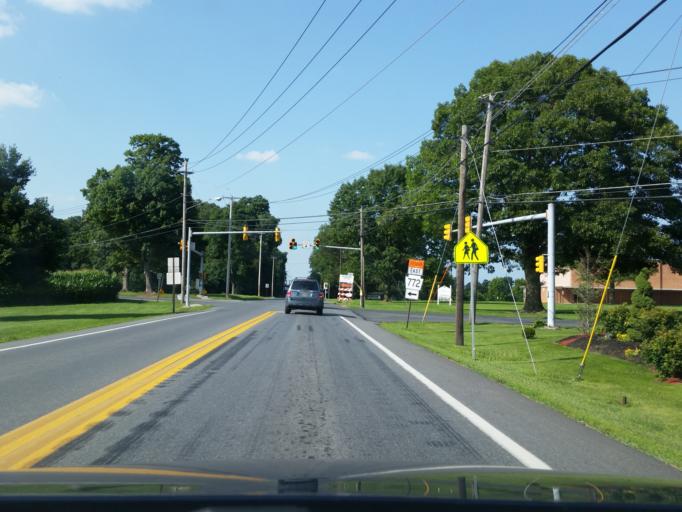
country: US
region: Pennsylvania
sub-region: Lancaster County
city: Mount Joy
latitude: 40.0910
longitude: -76.5200
